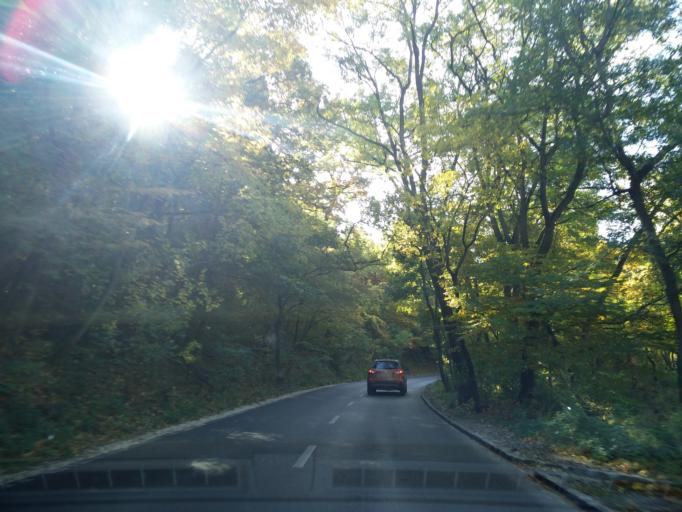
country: HU
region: Pest
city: Budakeszi
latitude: 47.5372
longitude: 18.9480
